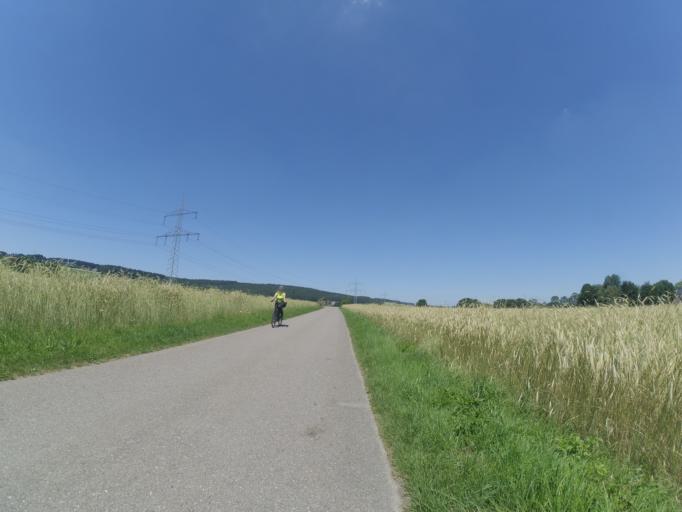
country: DE
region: Baden-Wuerttemberg
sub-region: Tuebingen Region
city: Bad Wurzach
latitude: 47.9033
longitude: 9.8467
